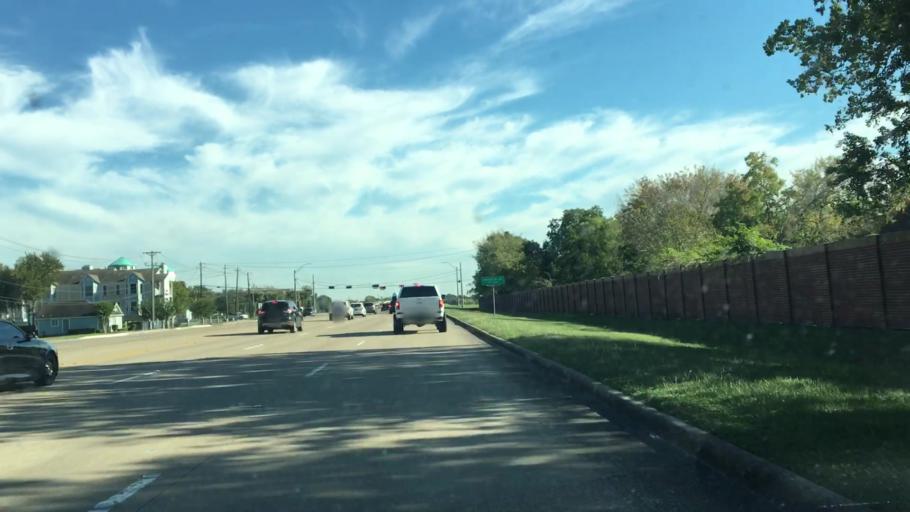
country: US
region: Texas
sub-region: Harris County
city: Nassau Bay
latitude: 29.5398
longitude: -95.1006
